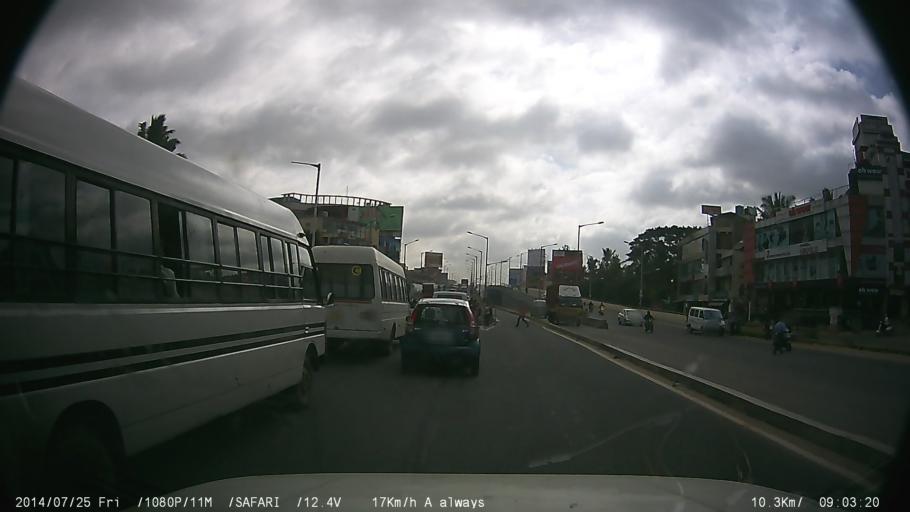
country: IN
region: Karnataka
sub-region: Bangalore Urban
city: Bangalore
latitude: 12.9249
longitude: 77.6743
